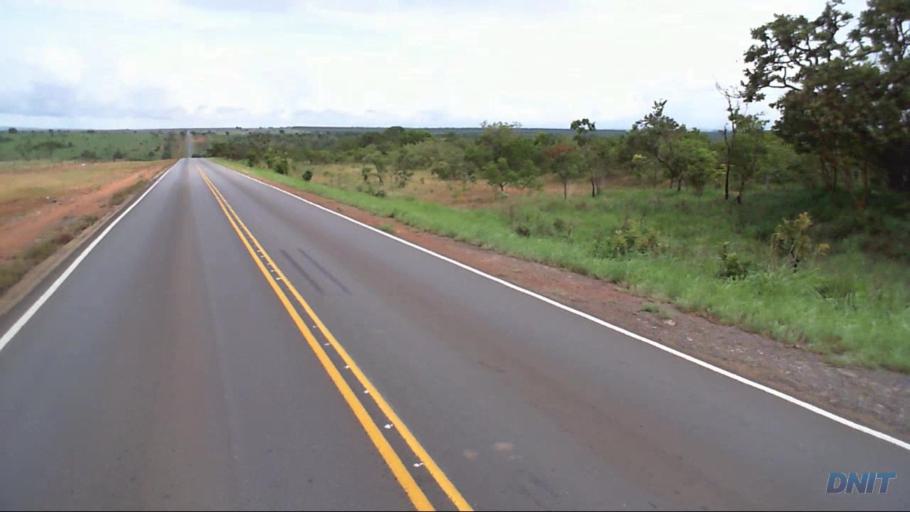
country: BR
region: Goias
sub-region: Padre Bernardo
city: Padre Bernardo
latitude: -15.3010
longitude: -48.2325
